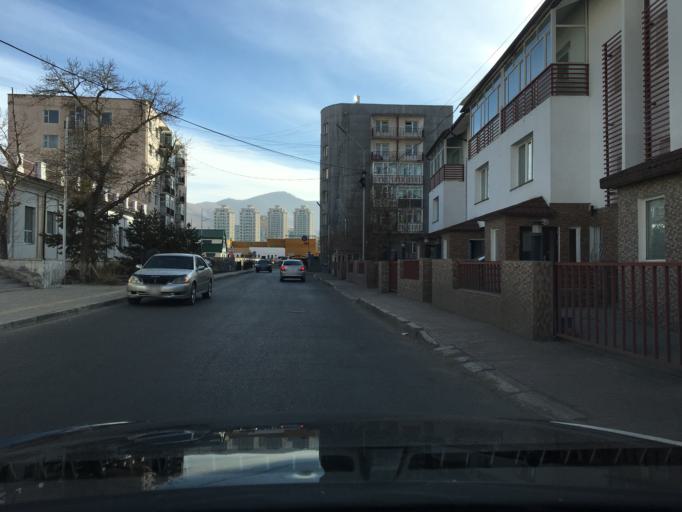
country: MN
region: Ulaanbaatar
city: Ulaanbaatar
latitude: 47.8958
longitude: 106.9134
